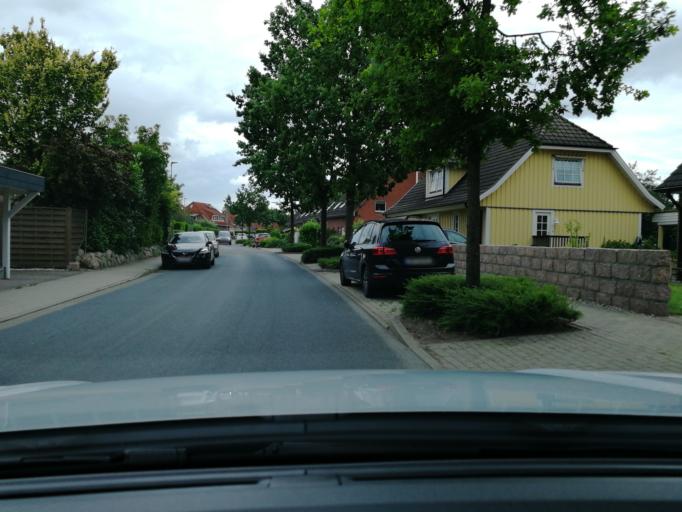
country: DE
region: Schleswig-Holstein
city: Schwarzenbek
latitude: 53.5121
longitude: 10.4856
